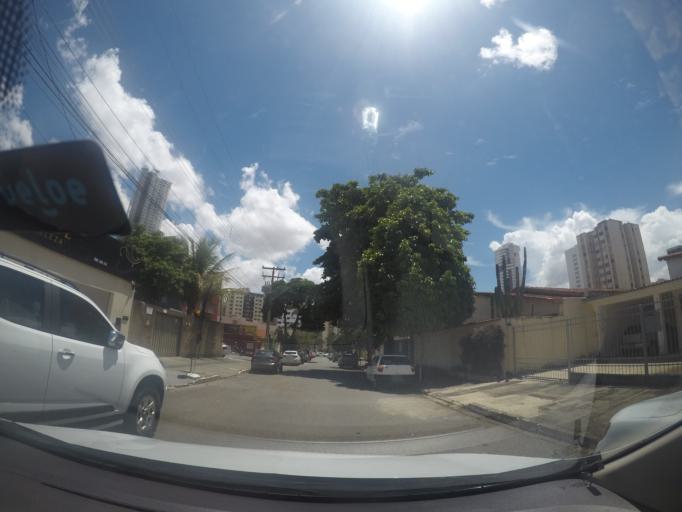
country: BR
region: Goias
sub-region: Goiania
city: Goiania
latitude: -16.7155
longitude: -49.2725
